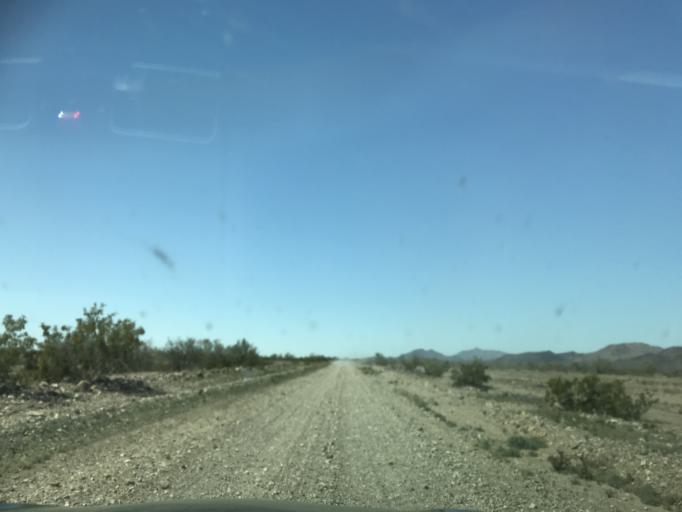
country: US
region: California
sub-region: Riverside County
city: Mesa Verde
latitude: 33.4786
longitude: -114.9364
